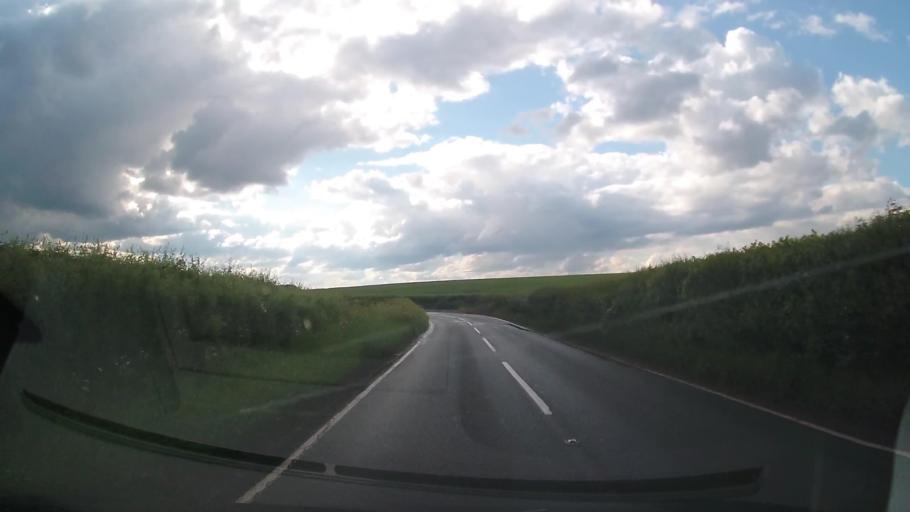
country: GB
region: England
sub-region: Shropshire
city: Withington
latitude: 52.6706
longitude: -2.6348
